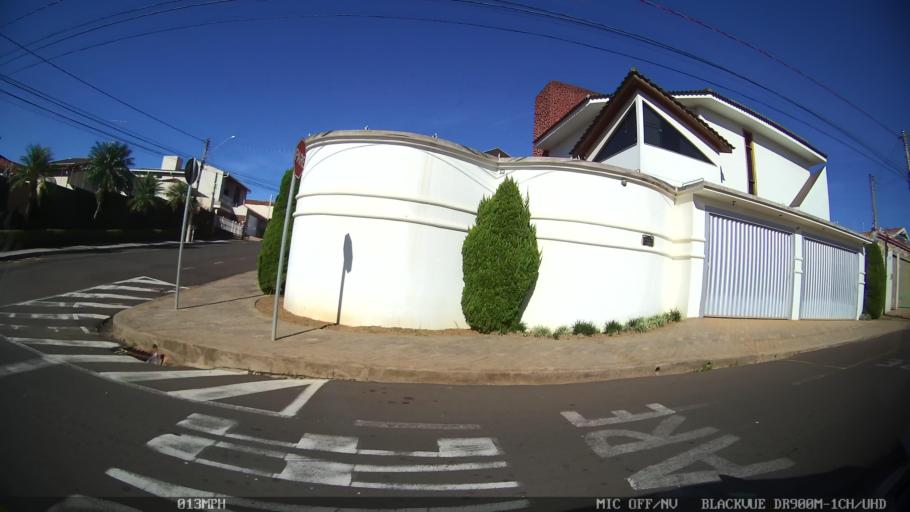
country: BR
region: Sao Paulo
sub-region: Franca
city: Franca
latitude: -20.5308
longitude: -47.4103
